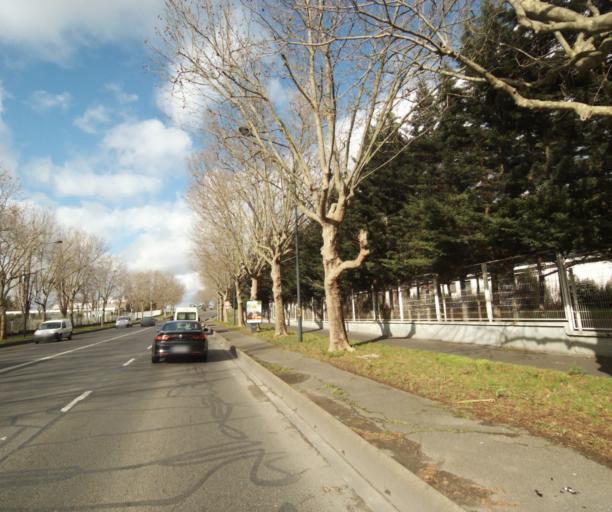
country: FR
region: Ile-de-France
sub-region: Departement de Seine-Saint-Denis
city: Saint-Denis
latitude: 48.9429
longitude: 2.3640
